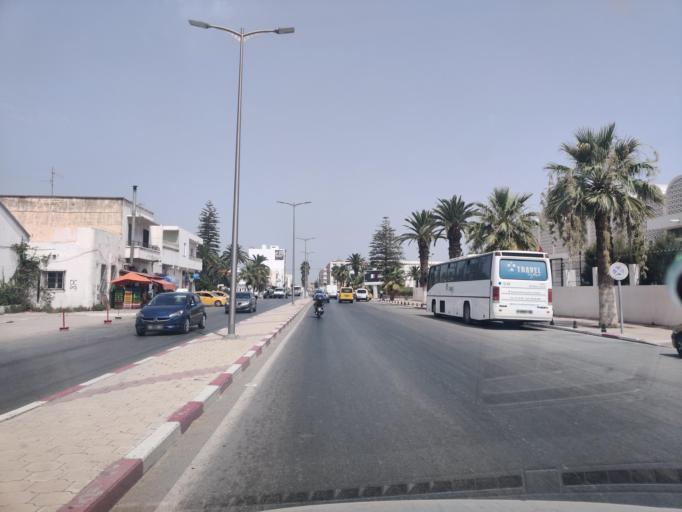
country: TN
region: Nabul
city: Bu `Urqub
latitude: 36.5965
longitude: 10.5004
